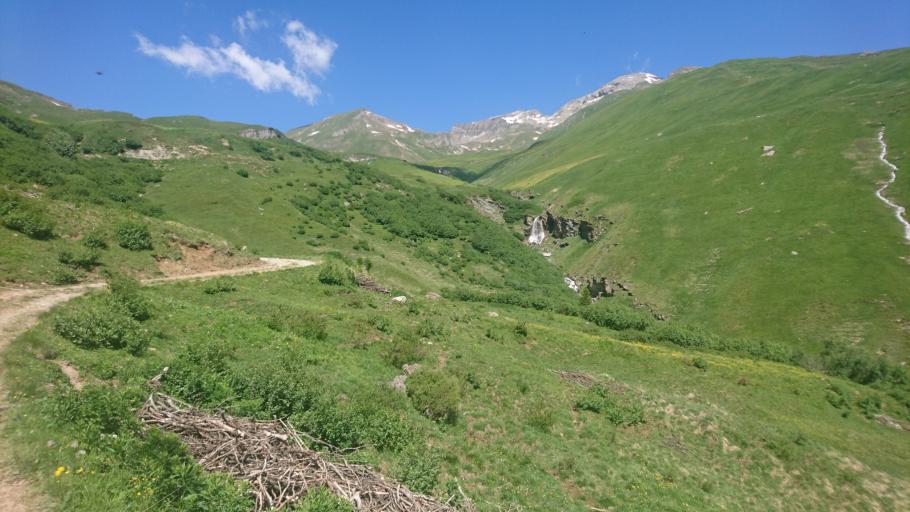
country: CH
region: Grisons
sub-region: Hinterrhein District
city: Thusis
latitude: 46.6290
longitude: 9.3817
